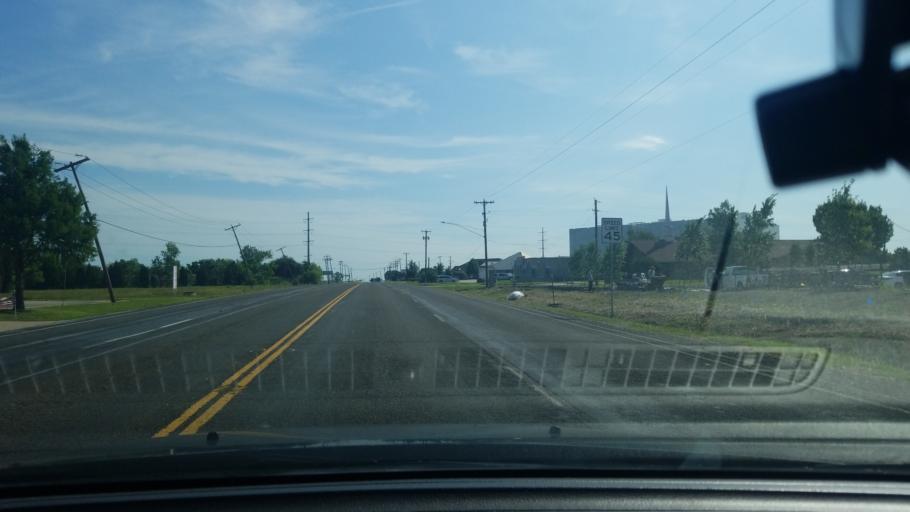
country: US
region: Texas
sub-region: Dallas County
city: Sunnyvale
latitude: 32.7727
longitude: -96.5726
